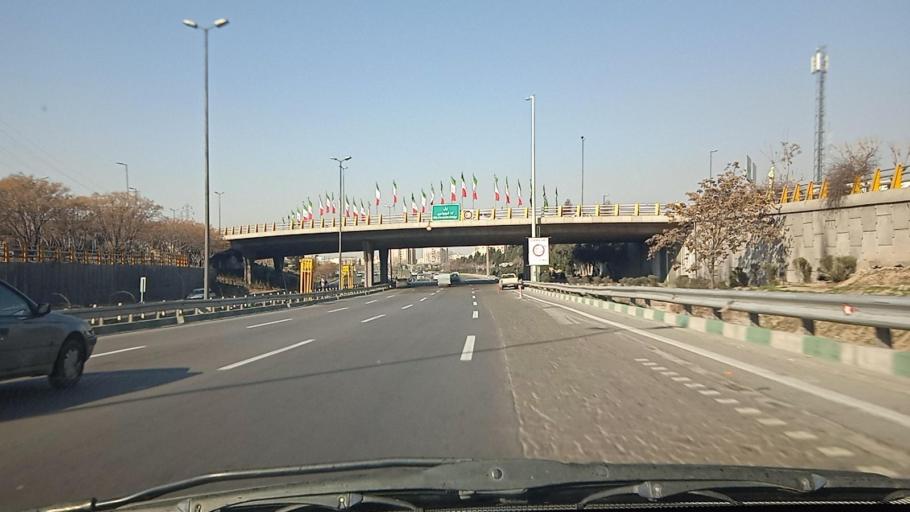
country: IR
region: Tehran
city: Tehran
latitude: 35.7223
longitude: 51.5240
